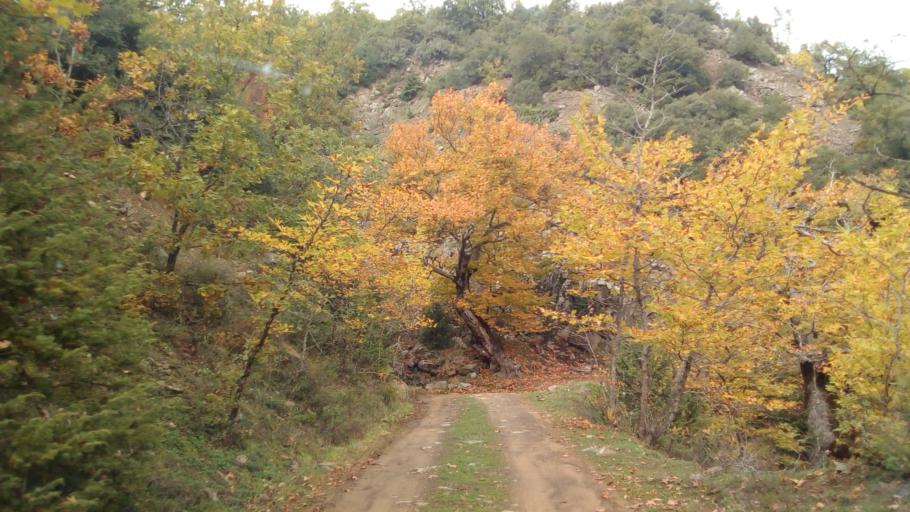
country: GR
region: West Greece
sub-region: Nomos Aitolias kai Akarnanias
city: Nafpaktos
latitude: 38.5538
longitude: 21.9660
